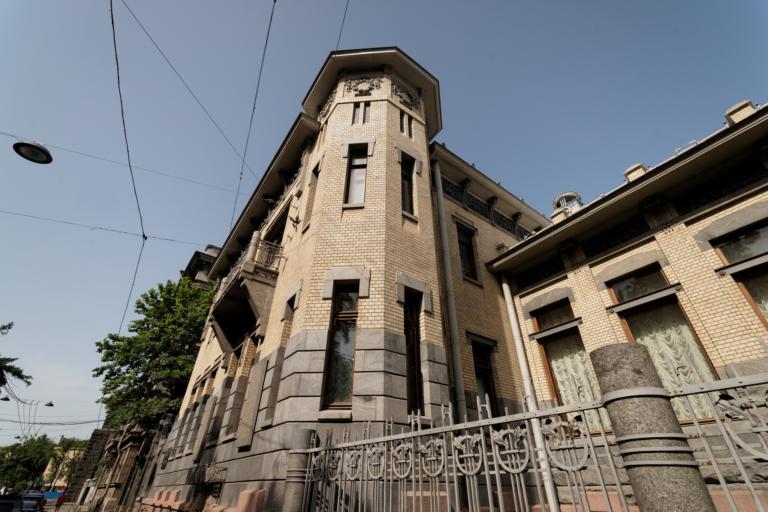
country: RU
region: St.-Petersburg
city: Petrogradka
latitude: 59.9542
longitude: 30.3245
